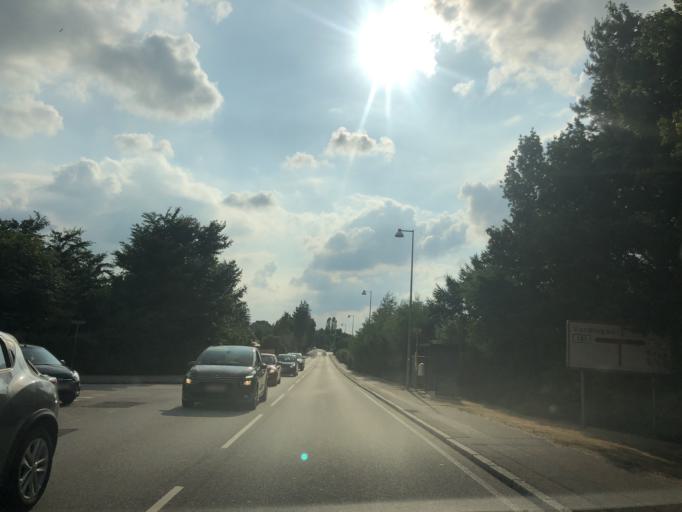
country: DK
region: Zealand
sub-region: Faxe Kommune
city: Ronnede
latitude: 55.3115
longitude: 12.0554
